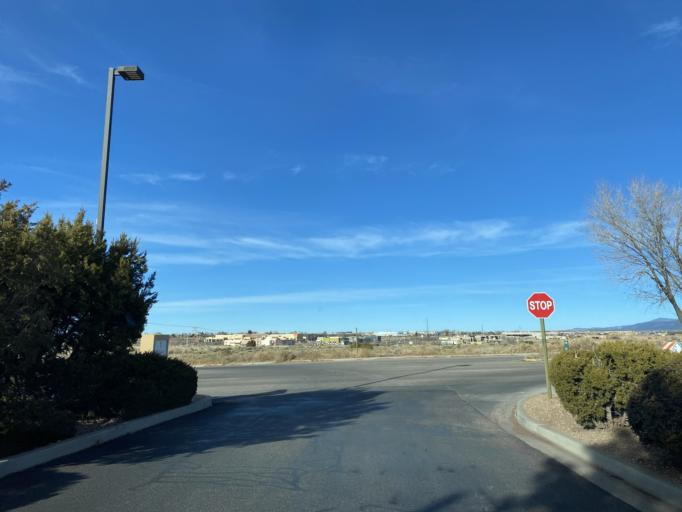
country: US
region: New Mexico
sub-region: Santa Fe County
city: Agua Fria
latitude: 35.6121
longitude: -106.0315
